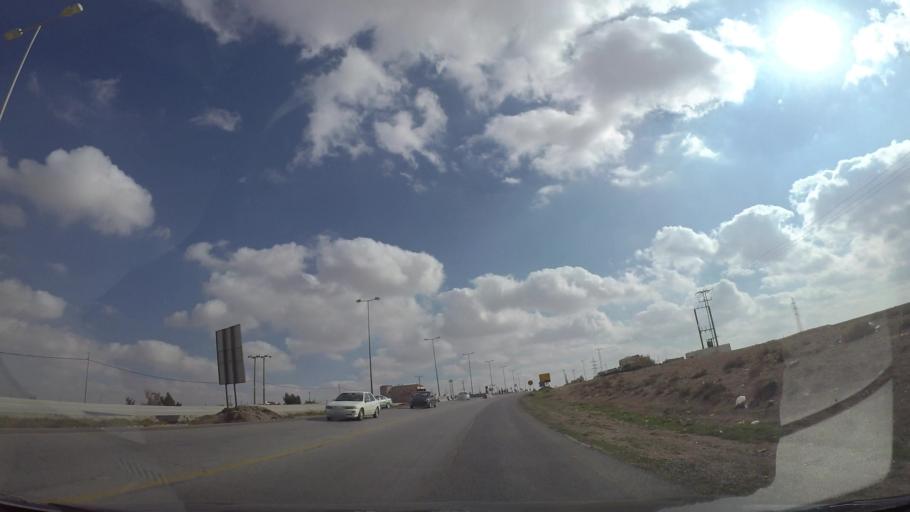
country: JO
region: Amman
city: Al Jizah
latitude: 31.6099
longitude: 36.0000
